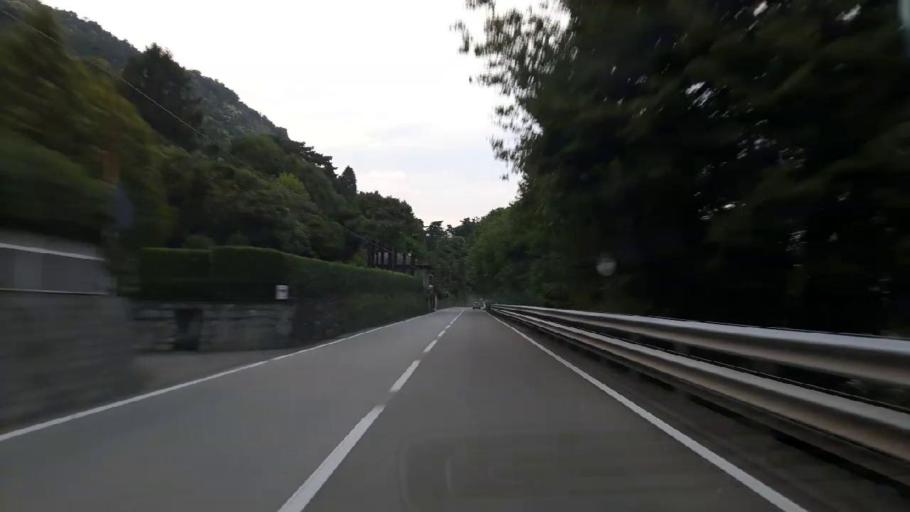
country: IT
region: Piedmont
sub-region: Provincia Verbano-Cusio-Ossola
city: Belgirate
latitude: 45.8551
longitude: 8.5690
